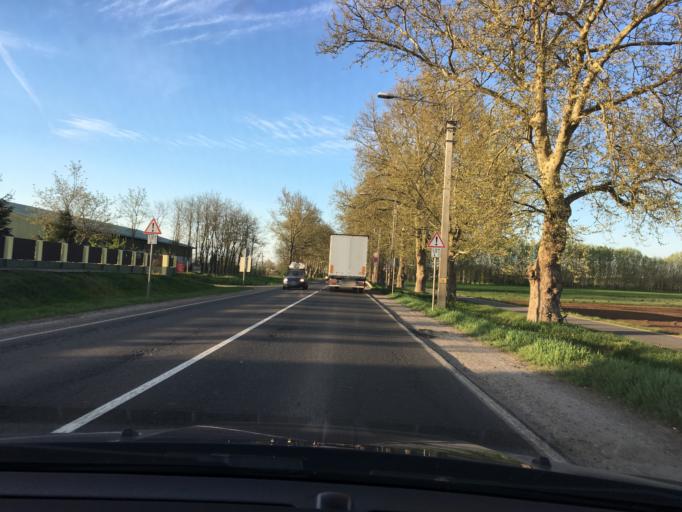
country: HU
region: Hajdu-Bihar
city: Mikepercs
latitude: 47.4540
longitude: 21.6345
